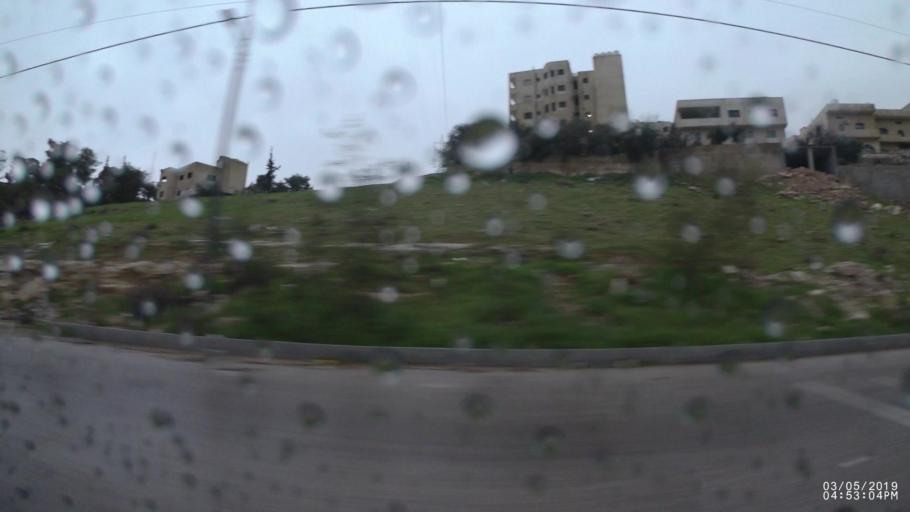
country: JO
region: Amman
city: Amman
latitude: 31.9916
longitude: 35.9745
